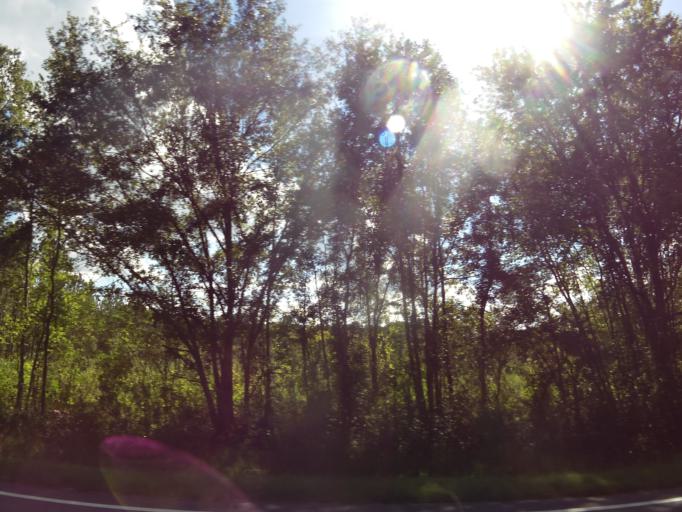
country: US
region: Georgia
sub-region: Lowndes County
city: Valdosta
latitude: 30.7941
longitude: -83.1847
